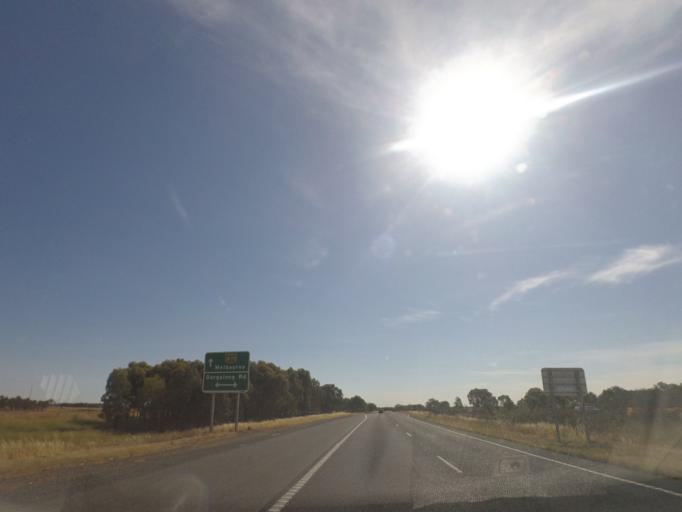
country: AU
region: Victoria
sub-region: Greater Shepparton
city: Shepparton
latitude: -36.6727
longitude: 145.2607
